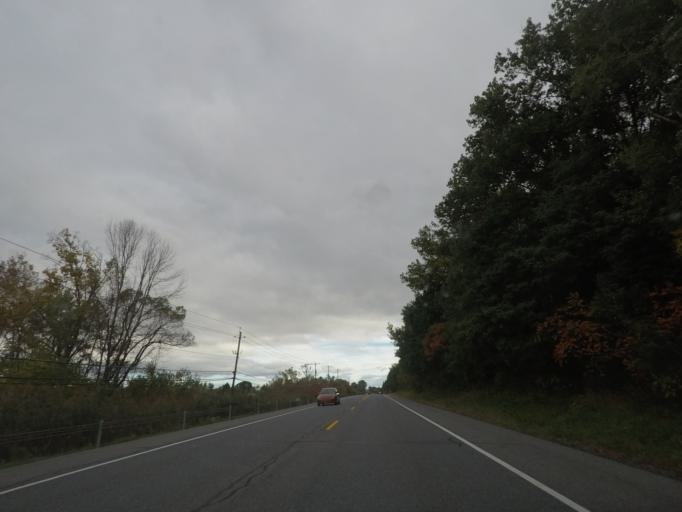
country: US
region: New York
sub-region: Saratoga County
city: Mechanicville
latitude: 42.8753
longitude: -73.7241
